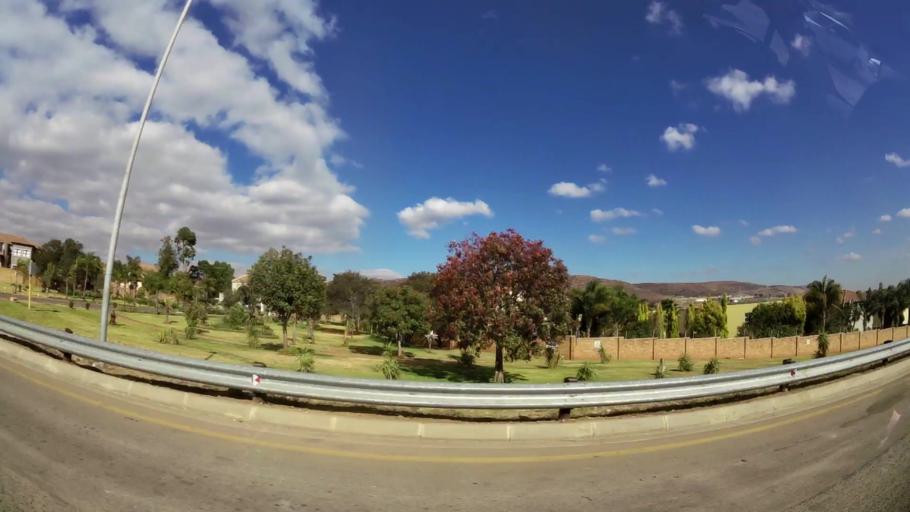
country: ZA
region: Gauteng
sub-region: West Rand District Municipality
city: Muldersdriseloop
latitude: -26.0689
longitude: 27.8500
